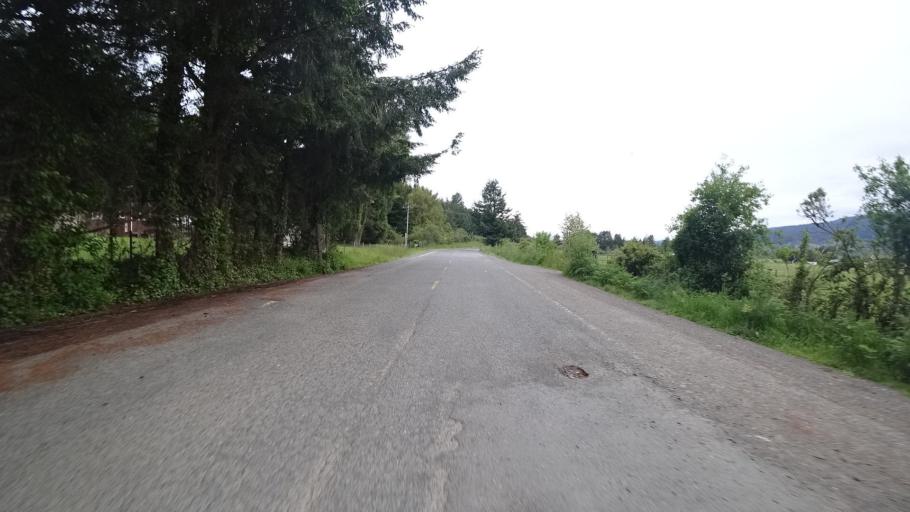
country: US
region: California
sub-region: Humboldt County
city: Blue Lake
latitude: 40.8574
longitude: -123.9948
